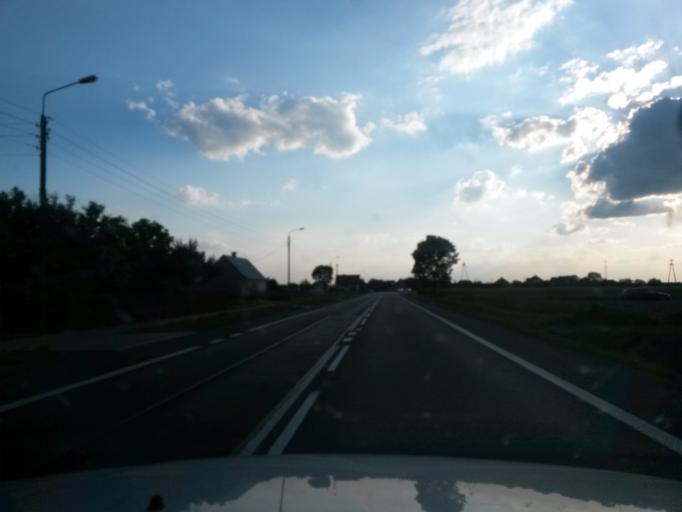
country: PL
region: Lodz Voivodeship
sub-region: Powiat wielunski
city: Osjakow
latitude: 51.3021
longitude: 18.8549
